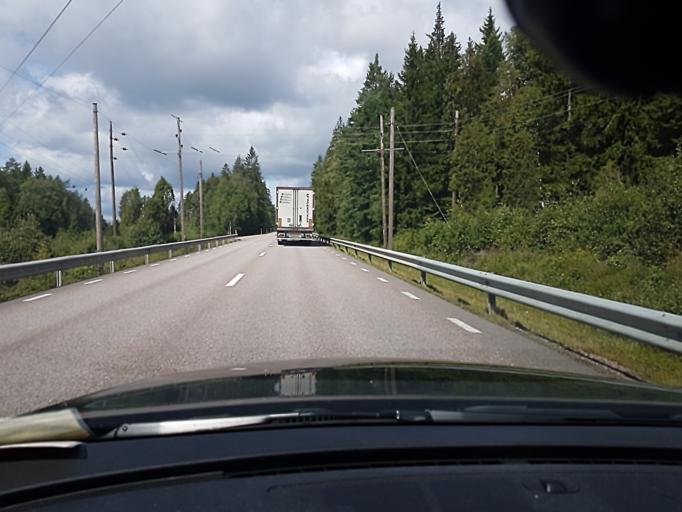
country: SE
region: Kronoberg
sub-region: Lessebo Kommun
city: Hovmantorp
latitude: 56.7835
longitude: 15.1947
